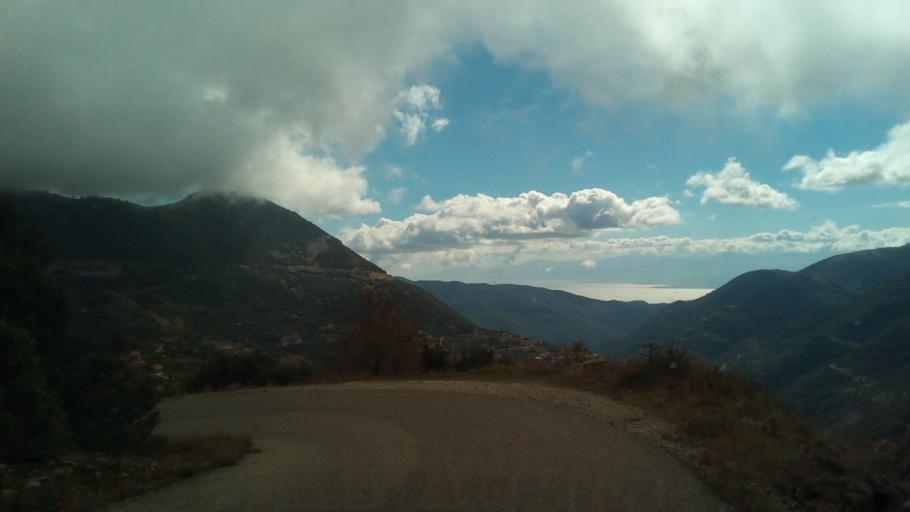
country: GR
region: West Greece
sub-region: Nomos Aitolias kai Akarnanias
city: Nafpaktos
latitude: 38.4989
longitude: 21.8357
